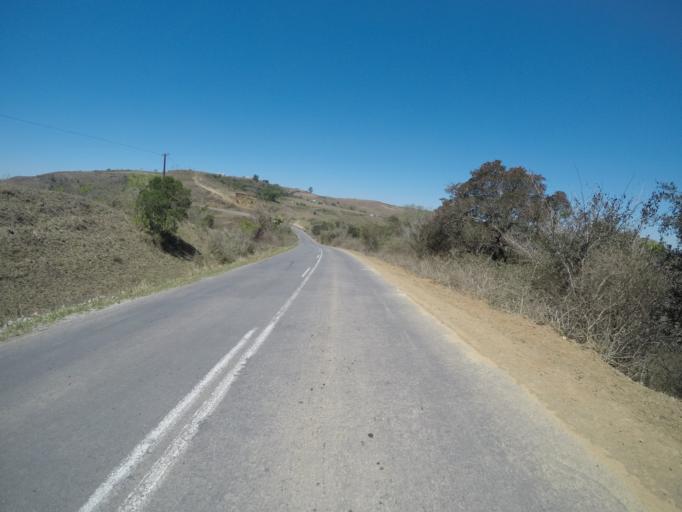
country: ZA
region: Eastern Cape
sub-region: OR Tambo District Municipality
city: Mthatha
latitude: -31.9141
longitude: 28.9611
